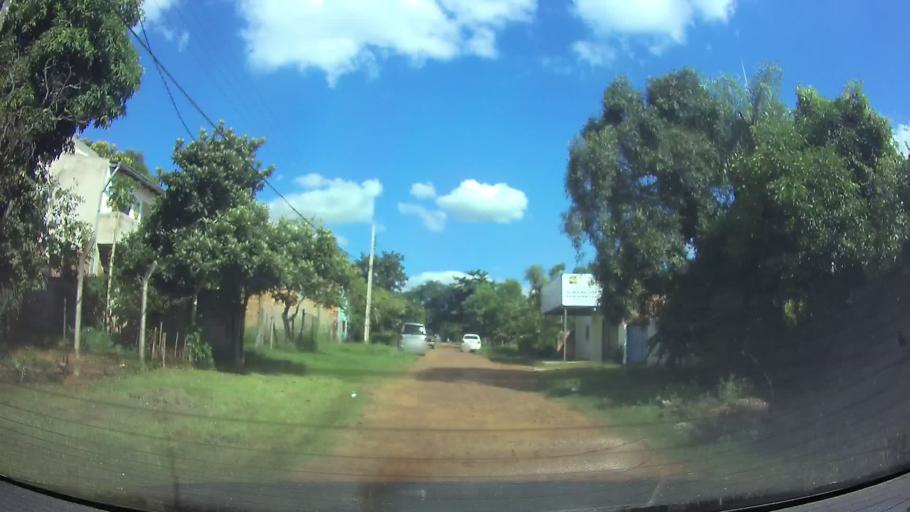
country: PY
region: Central
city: Itaugua
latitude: -25.3869
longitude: -57.3467
